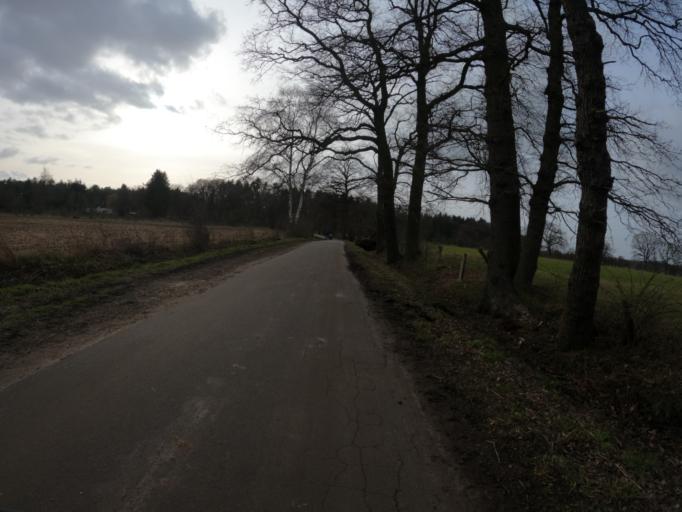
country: DE
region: Schleswig-Holstein
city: Appen
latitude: 53.6061
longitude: 9.7730
